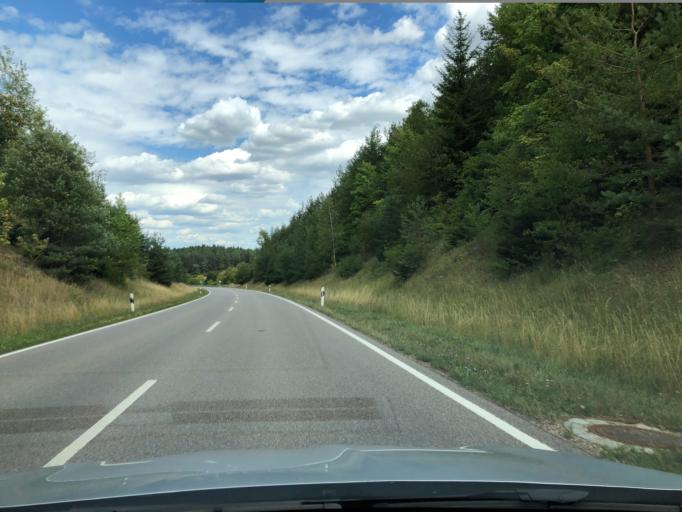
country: DE
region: Bavaria
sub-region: Upper Palatinate
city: Illschwang
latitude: 49.4664
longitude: 11.7031
